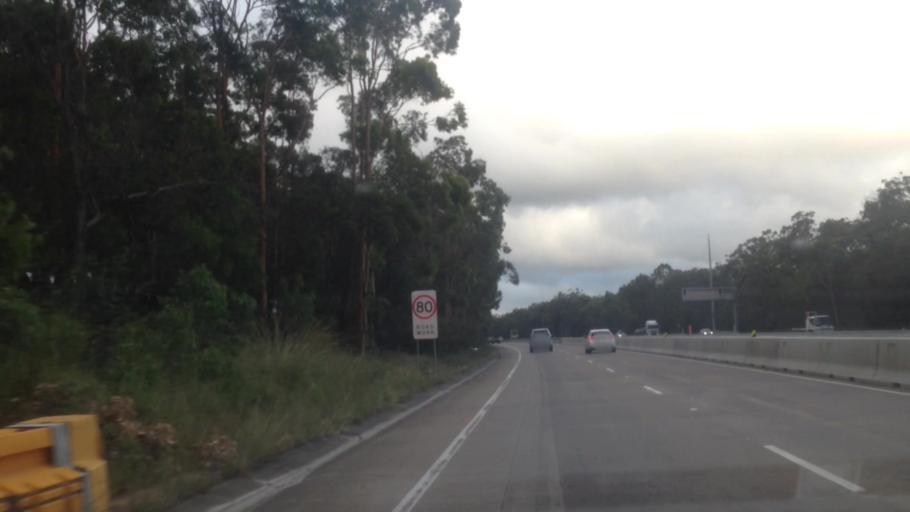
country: AU
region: New South Wales
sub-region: Wyong Shire
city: Jilliby
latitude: -33.2185
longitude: 151.4422
